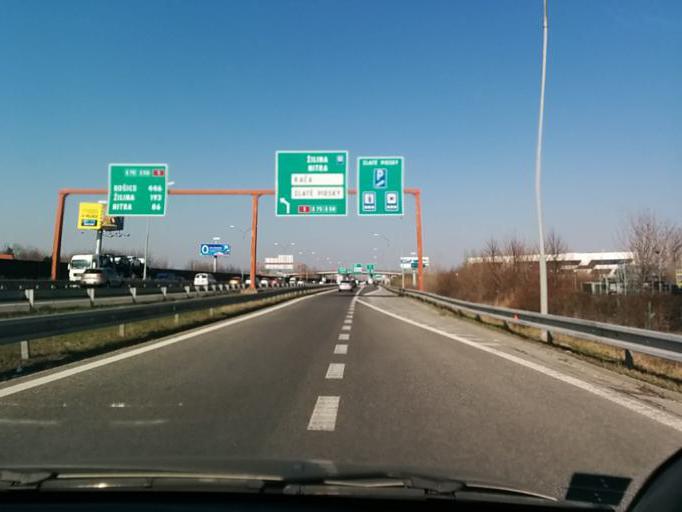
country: SK
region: Bratislavsky
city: Svaty Jur
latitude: 48.1727
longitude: 17.1875
